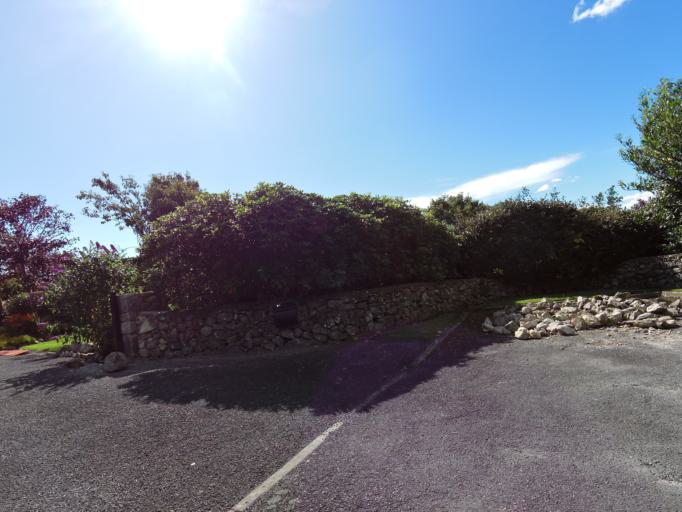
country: IE
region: Connaught
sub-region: County Galway
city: Gaillimh
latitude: 53.2868
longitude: -9.0854
